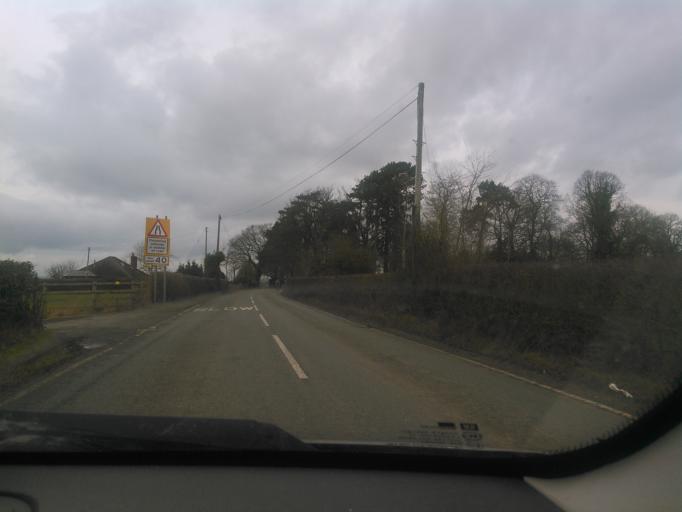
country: GB
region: England
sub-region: Shropshire
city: Wem
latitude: 52.8381
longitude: -2.7062
